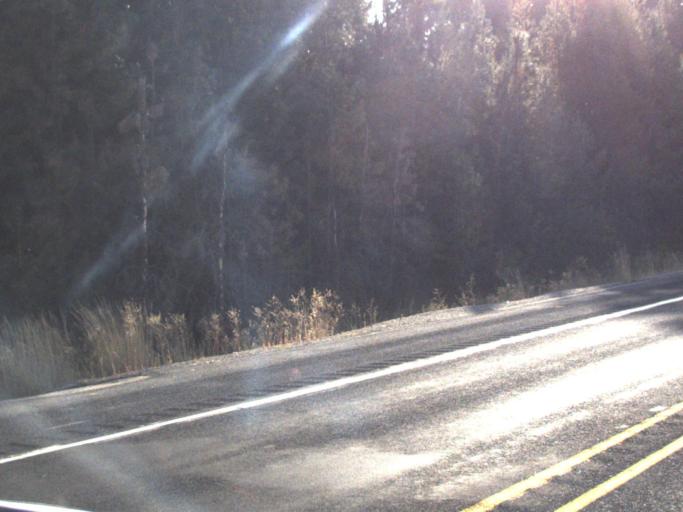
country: US
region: Washington
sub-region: Pend Oreille County
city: Newport
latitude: 48.0974
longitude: -117.2711
